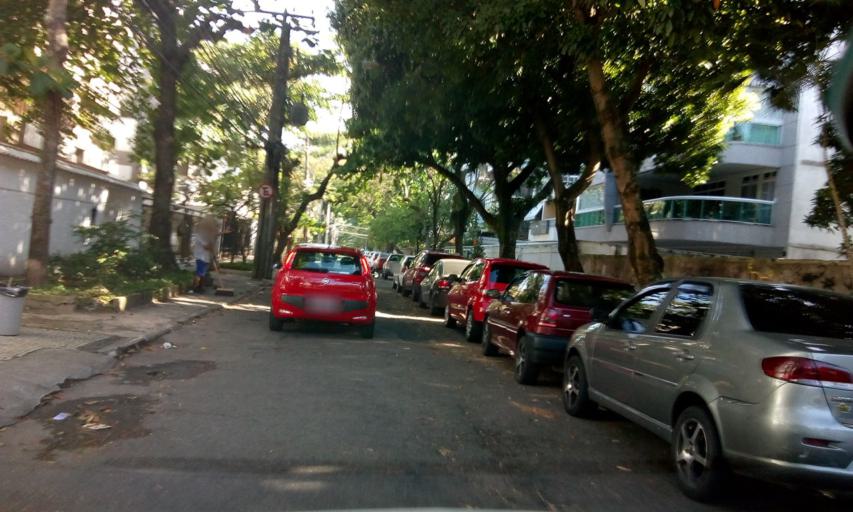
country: BR
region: Rio de Janeiro
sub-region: Rio De Janeiro
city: Rio de Janeiro
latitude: -23.0116
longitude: -43.3140
